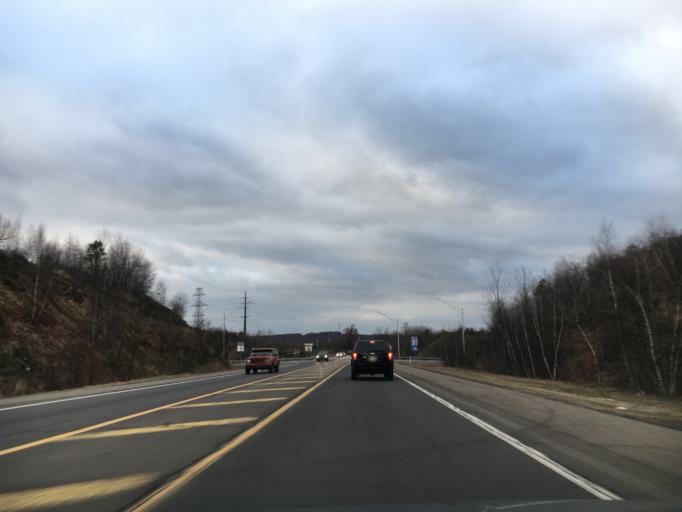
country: US
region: Pennsylvania
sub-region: Schuylkill County
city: McAdoo
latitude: 40.9255
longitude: -76.0089
